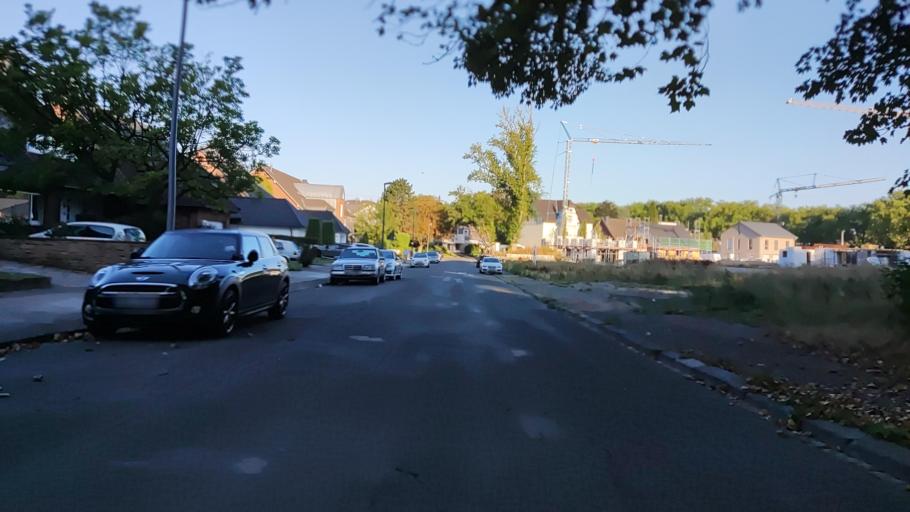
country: DE
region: North Rhine-Westphalia
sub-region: Regierungsbezirk Arnsberg
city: Herne
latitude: 51.5423
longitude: 7.2361
